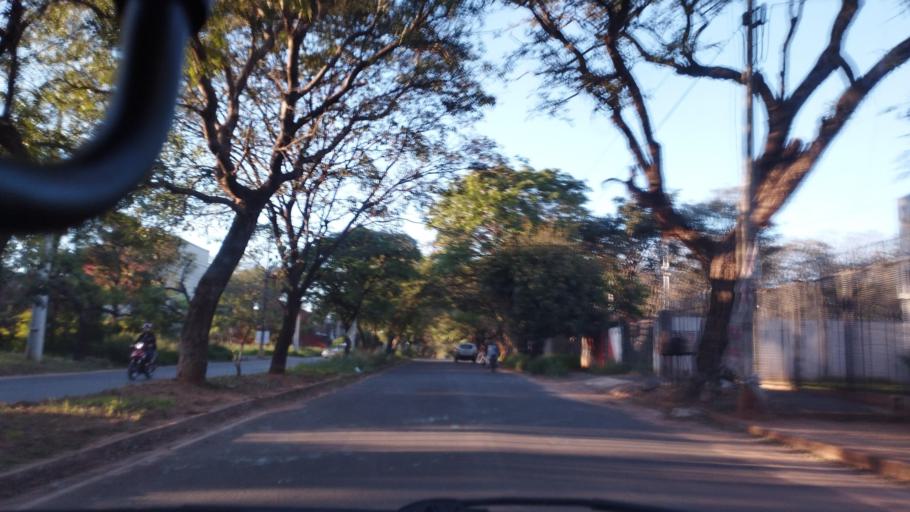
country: PY
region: Central
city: Fernando de la Mora
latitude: -25.2927
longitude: -57.5222
